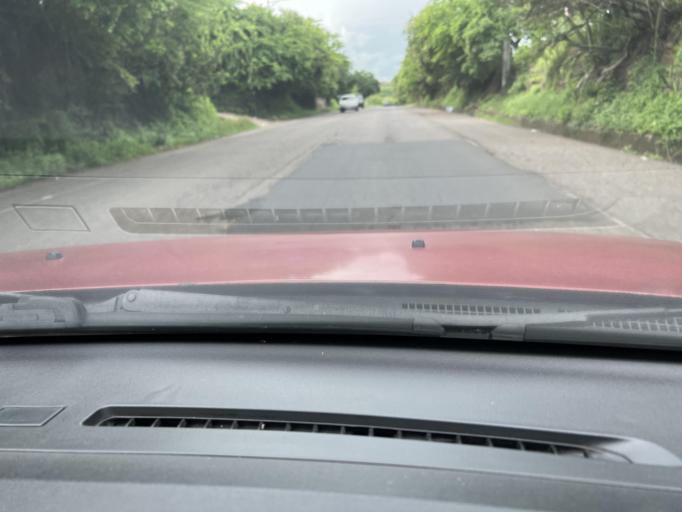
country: SV
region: La Union
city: San Alejo
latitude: 13.3969
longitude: -87.8993
